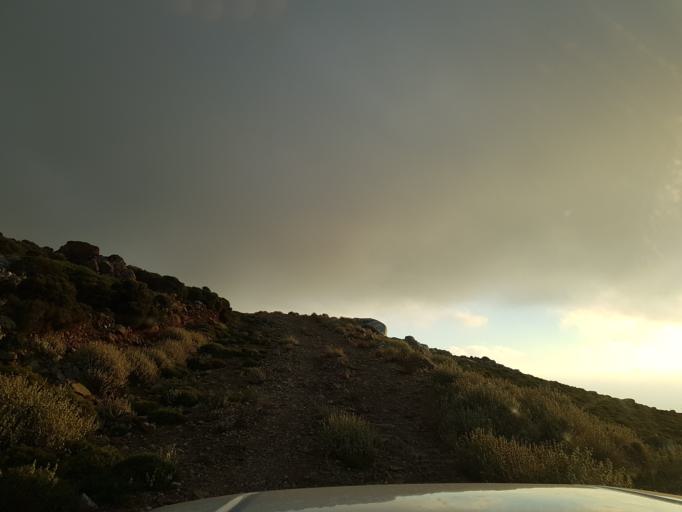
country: GR
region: Crete
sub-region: Nomos Chanias
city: Vryses
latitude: 35.4463
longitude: 23.5931
